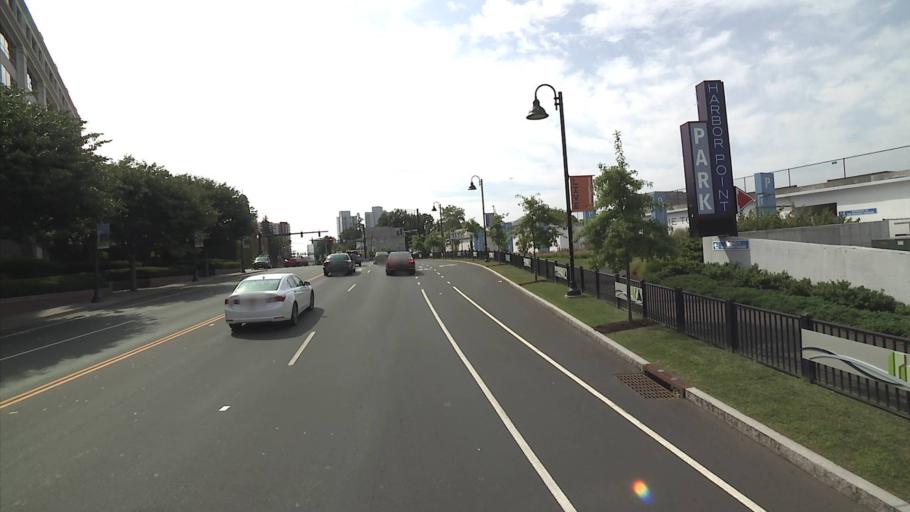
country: US
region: Connecticut
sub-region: Fairfield County
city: Stamford
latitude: 41.0459
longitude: -73.5431
